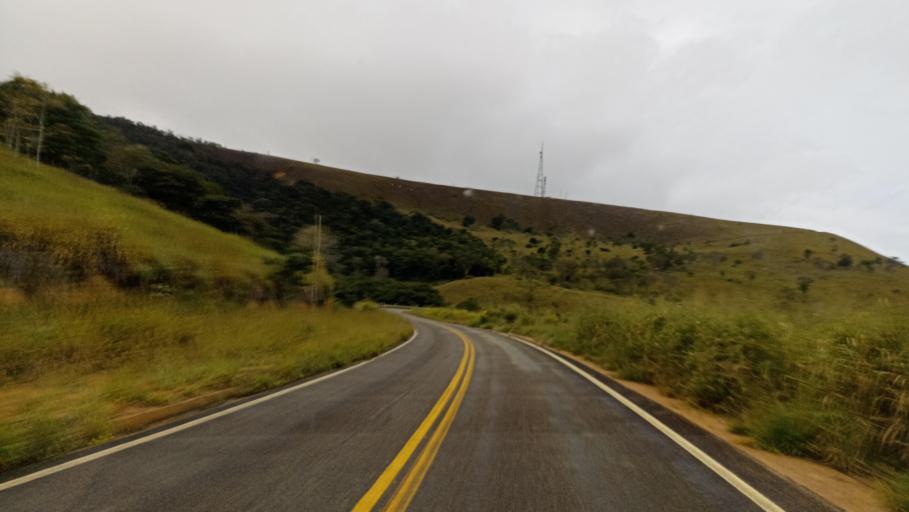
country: BR
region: Minas Gerais
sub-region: Joaima
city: Joaima
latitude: -16.6799
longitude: -40.5229
